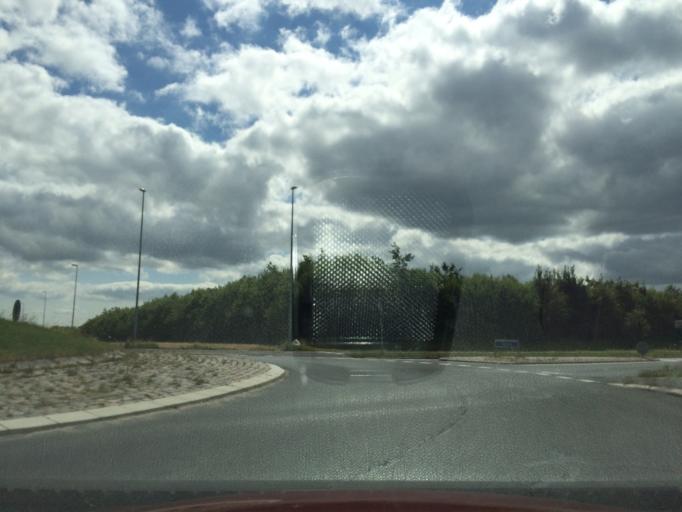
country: DK
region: Central Jutland
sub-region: Silkeborg Kommune
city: Svejbaek
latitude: 56.1912
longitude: 9.6086
